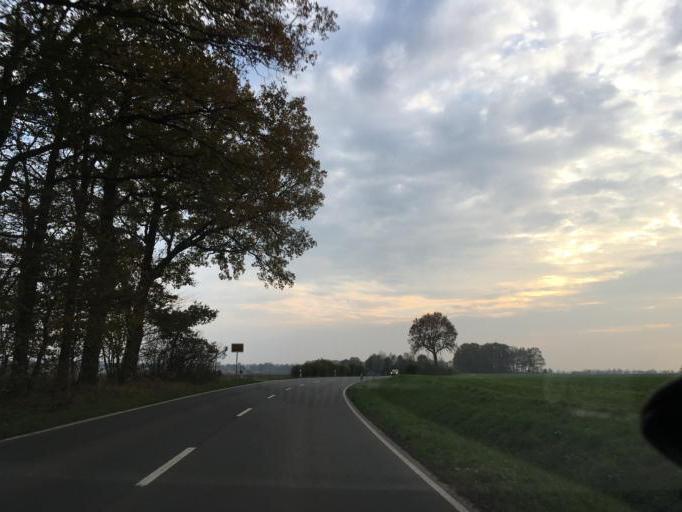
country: DE
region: Lower Saxony
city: Bergen
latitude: 52.8553
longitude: 9.9797
